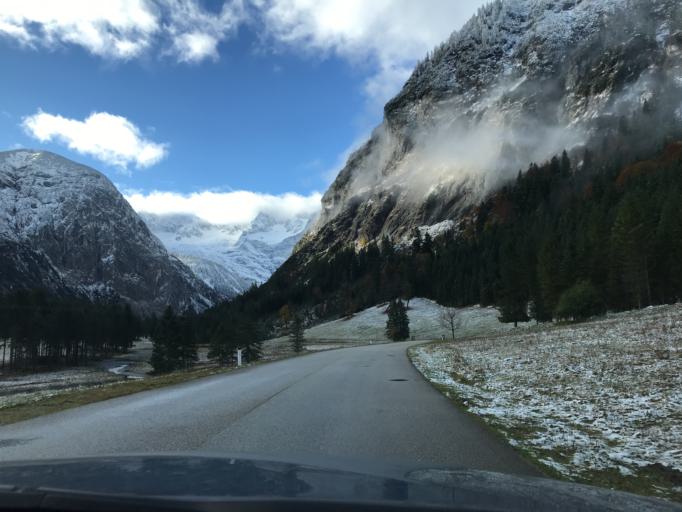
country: AT
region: Tyrol
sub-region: Politischer Bezirk Innsbruck Land
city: Gnadenwald
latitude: 47.4311
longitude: 11.5754
